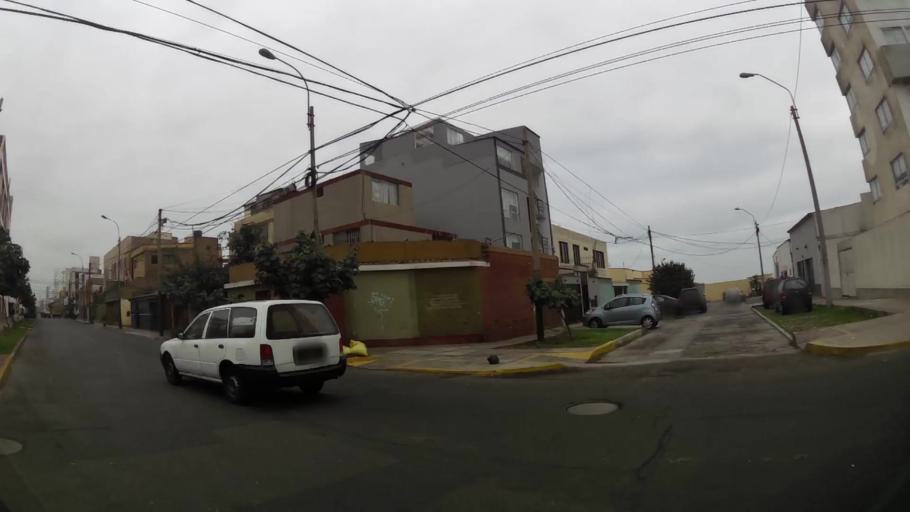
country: PE
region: Lima
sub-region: Lima
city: San Isidro
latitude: -12.0944
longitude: -77.0774
